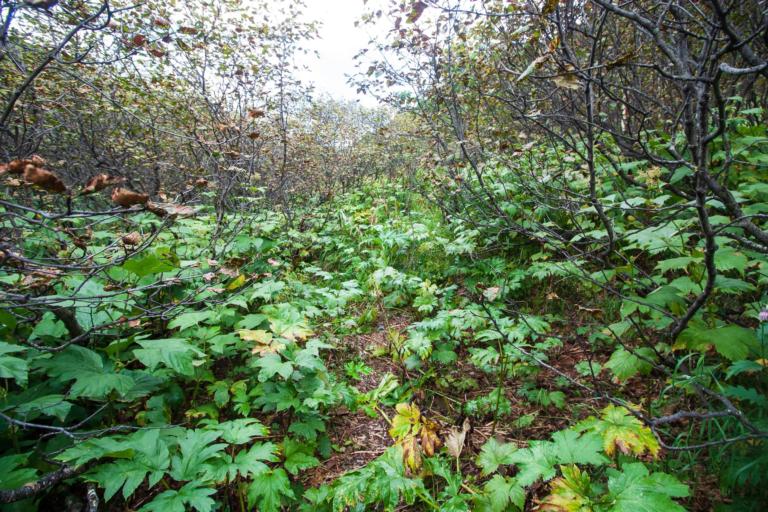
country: RU
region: Kamtsjatka
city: Yelizovo
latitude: 53.8190
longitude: 158.1477
